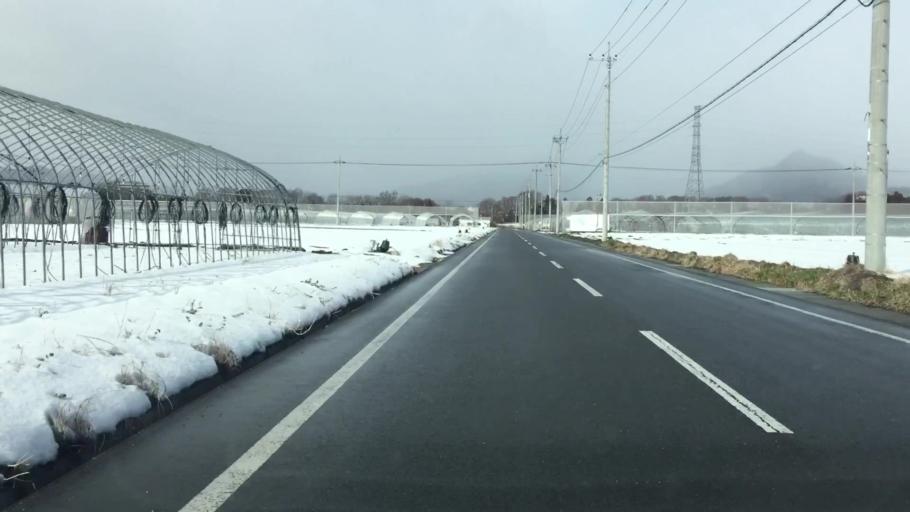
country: JP
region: Gunma
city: Numata
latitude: 36.6350
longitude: 139.0843
